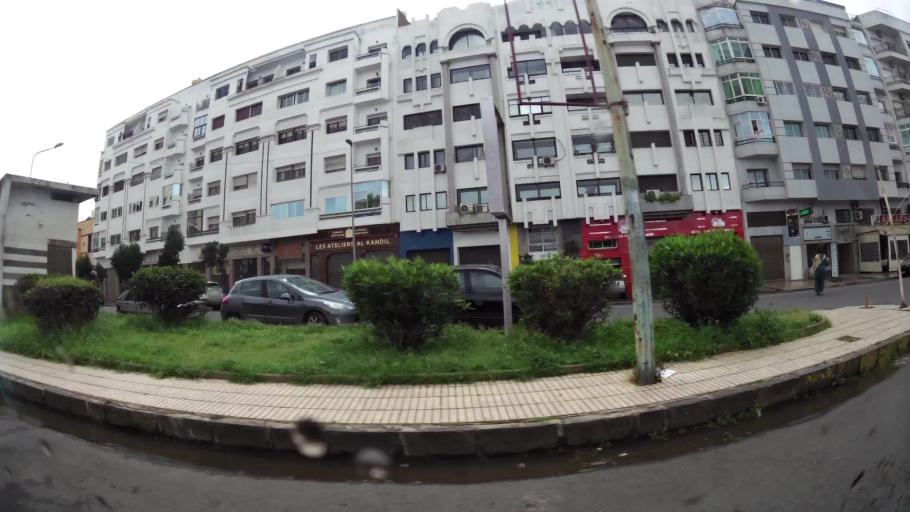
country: MA
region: Grand Casablanca
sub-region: Casablanca
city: Casablanca
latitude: 33.5723
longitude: -7.6238
